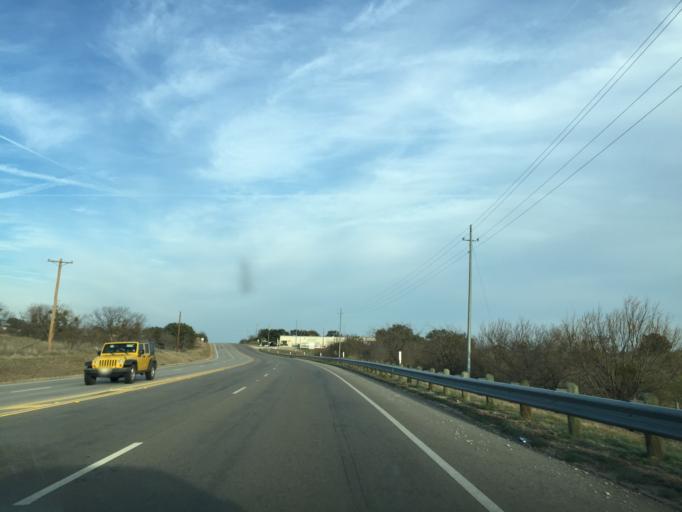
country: US
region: Texas
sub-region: Llano County
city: Llano
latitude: 30.7594
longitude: -98.6630
